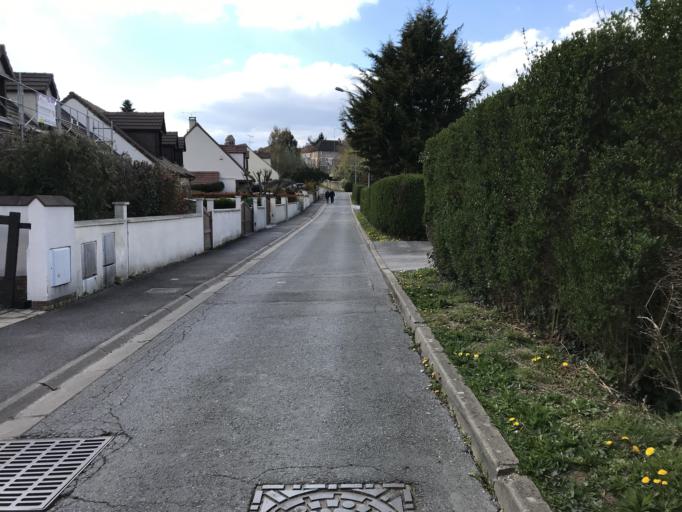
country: FR
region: Ile-de-France
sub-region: Departement de l'Essonne
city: Vauhallan
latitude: 48.7330
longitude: 2.2108
